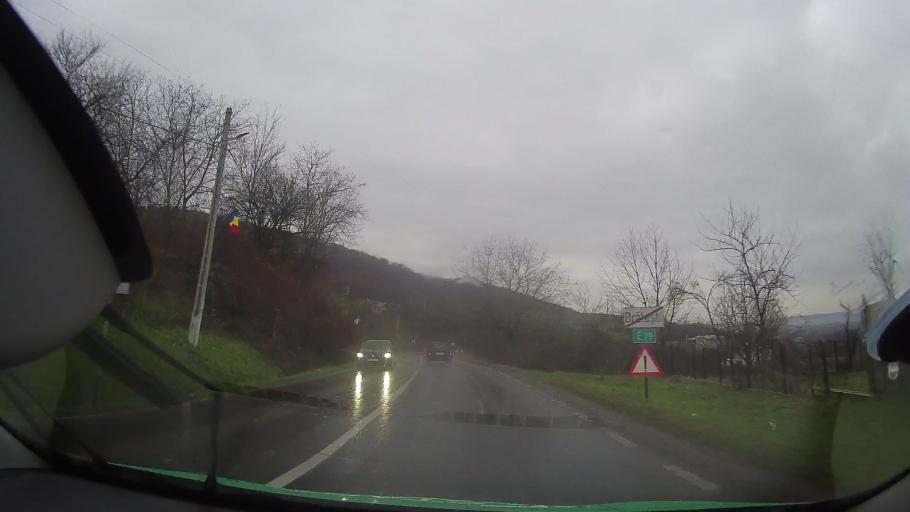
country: RO
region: Bihor
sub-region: Comuna Sambata
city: Sambata
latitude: 46.7626
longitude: 22.1891
